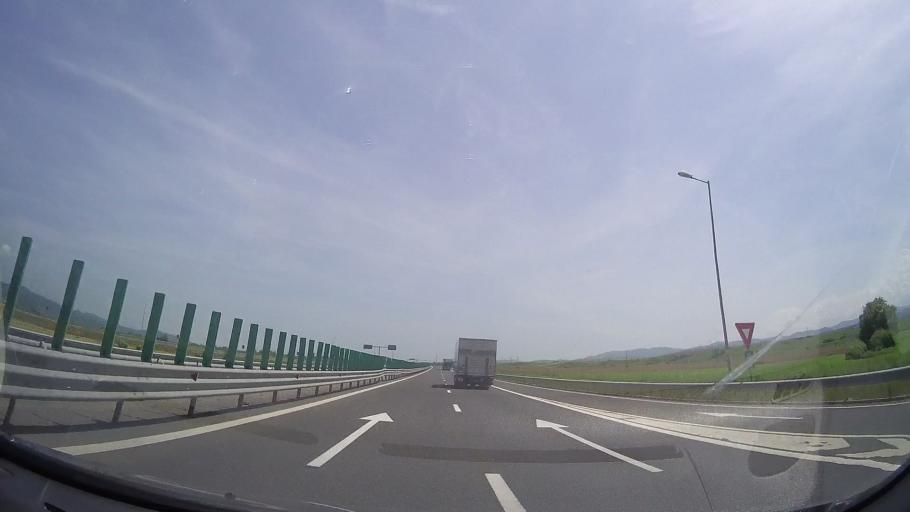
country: RO
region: Hunedoara
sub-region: Comuna Romos
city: Romos
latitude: 45.8907
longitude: 23.2656
